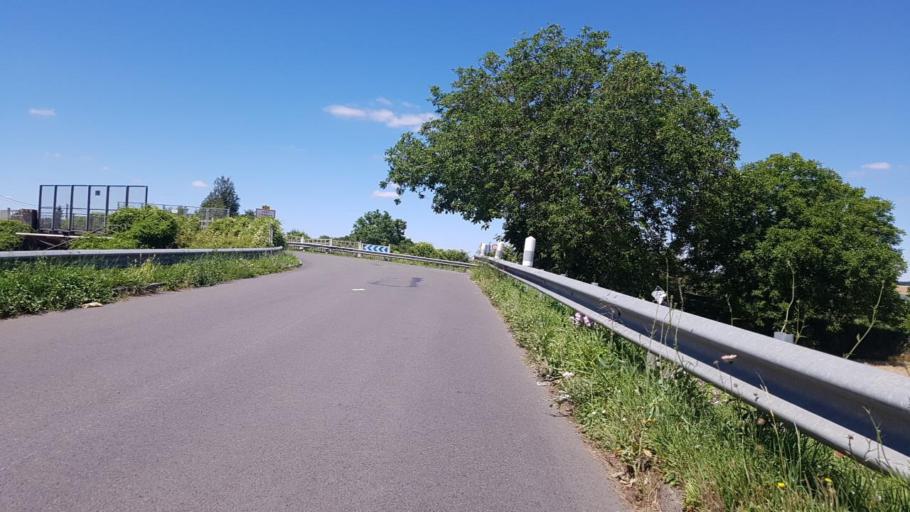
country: FR
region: Ile-de-France
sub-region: Departement de Seine-et-Marne
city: Sammeron
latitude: 48.9548
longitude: 3.0823
